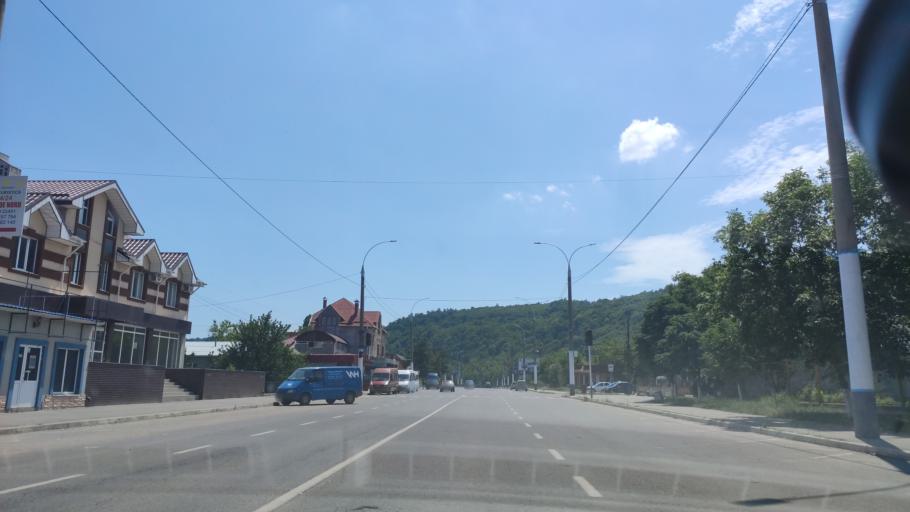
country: MD
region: Raionul Soroca
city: Soroca
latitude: 48.1477
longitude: 28.3021
